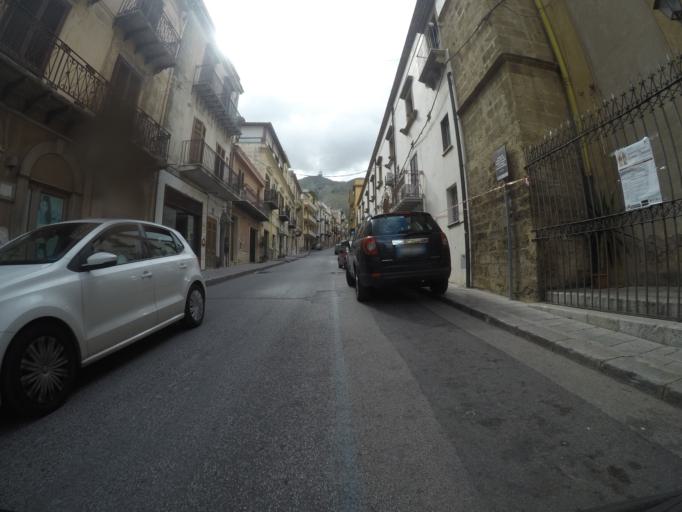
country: IT
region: Sicily
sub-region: Palermo
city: Carini
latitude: 38.1305
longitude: 13.1817
